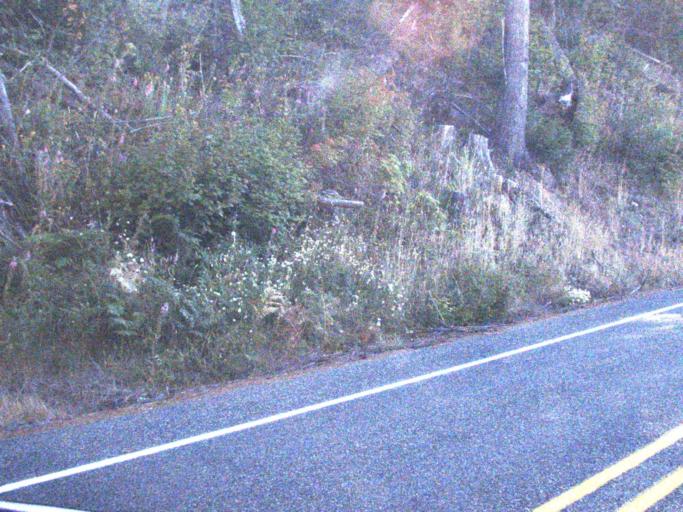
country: US
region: Washington
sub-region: King County
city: Enumclaw
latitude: 47.1532
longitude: -121.8528
